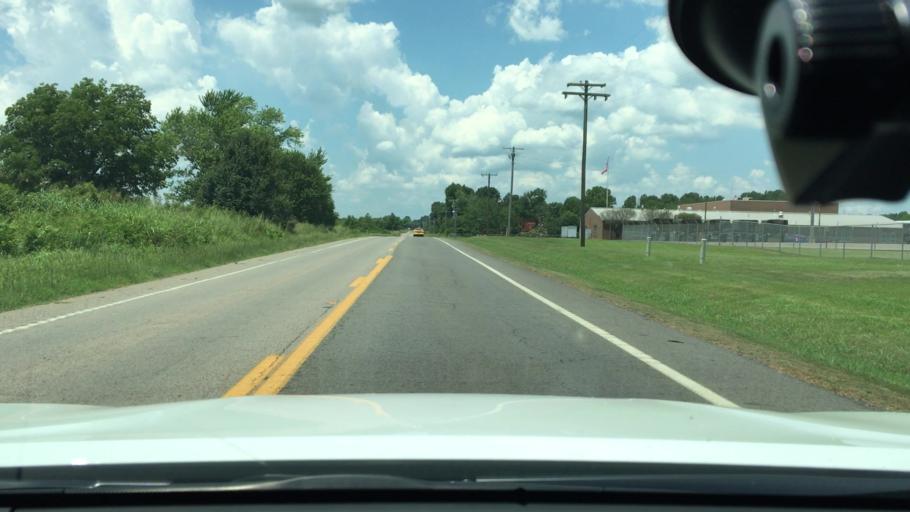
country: US
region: Arkansas
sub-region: Logan County
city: Booneville
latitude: 35.1478
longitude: -93.8671
